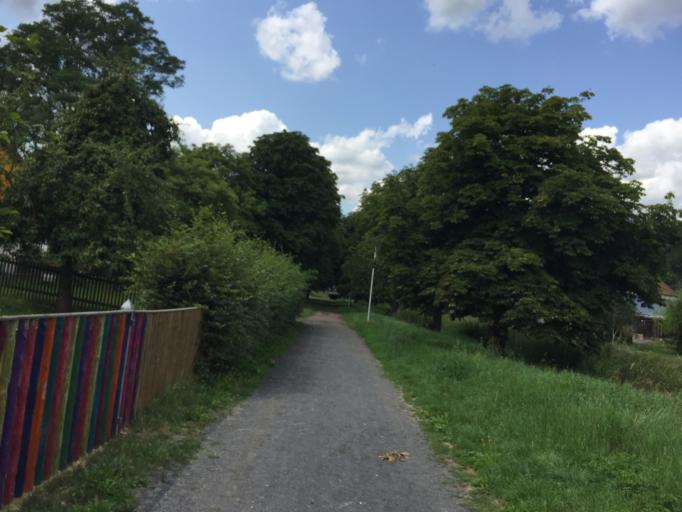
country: DE
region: Hesse
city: Schwalmstadt
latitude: 50.9157
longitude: 9.1874
